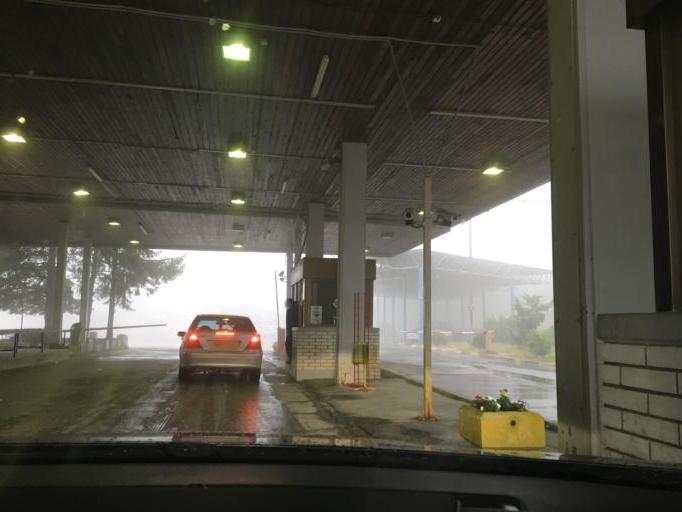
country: MK
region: Kriva Palanka
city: Kriva Palanka
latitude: 42.2204
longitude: 22.4592
